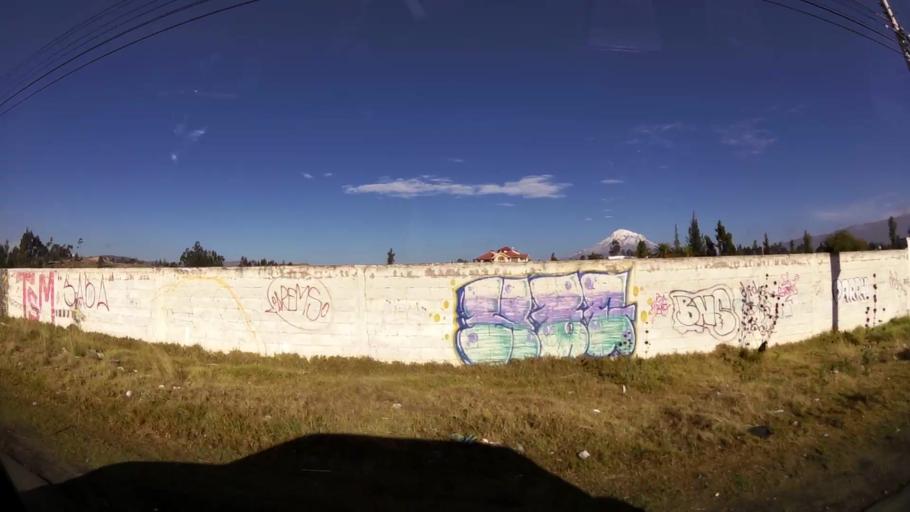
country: EC
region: Chimborazo
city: Riobamba
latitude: -1.6433
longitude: -78.6400
